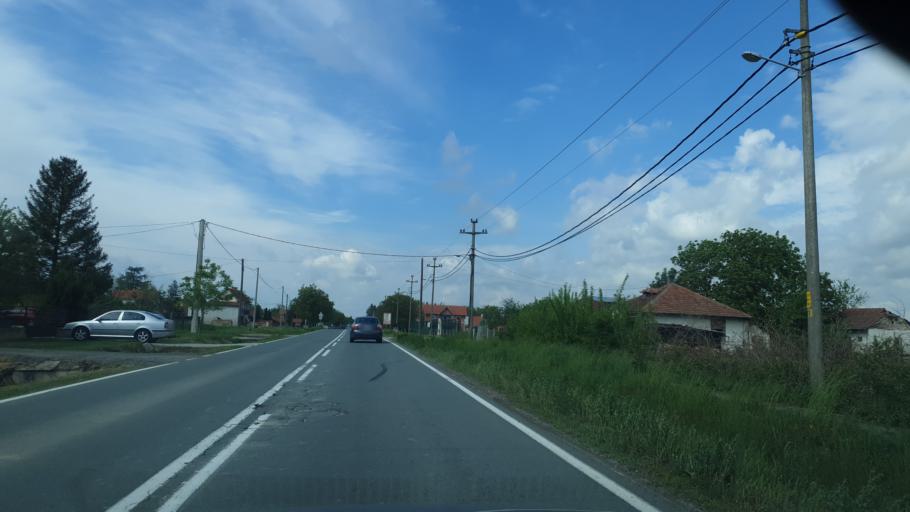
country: RS
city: Stubline
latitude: 44.5587
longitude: 20.1475
